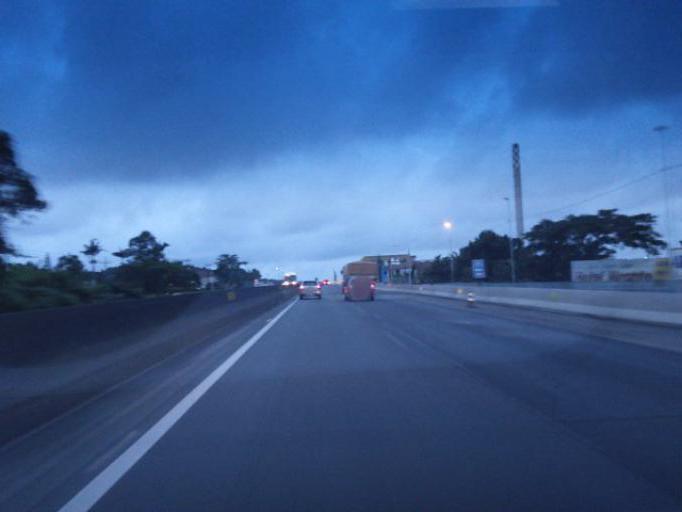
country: BR
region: Santa Catarina
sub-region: Barra Velha
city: Barra Velha
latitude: -26.6268
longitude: -48.7102
